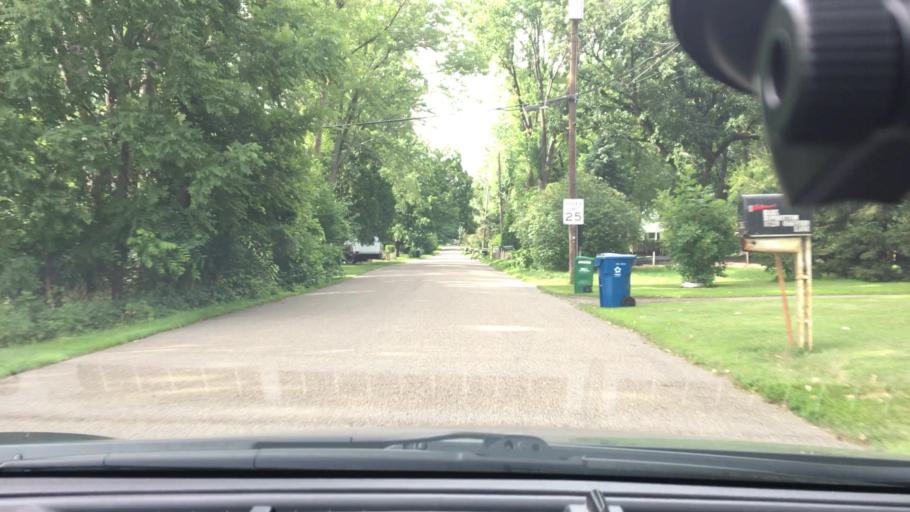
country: US
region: Minnesota
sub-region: Hennepin County
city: Plymouth
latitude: 44.9982
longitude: -93.4399
